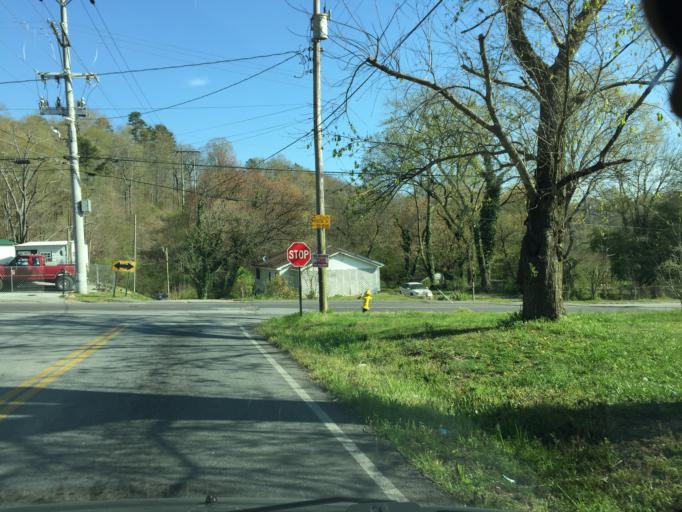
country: US
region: Tennessee
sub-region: Hamilton County
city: East Chattanooga
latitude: 35.0675
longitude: -85.2282
